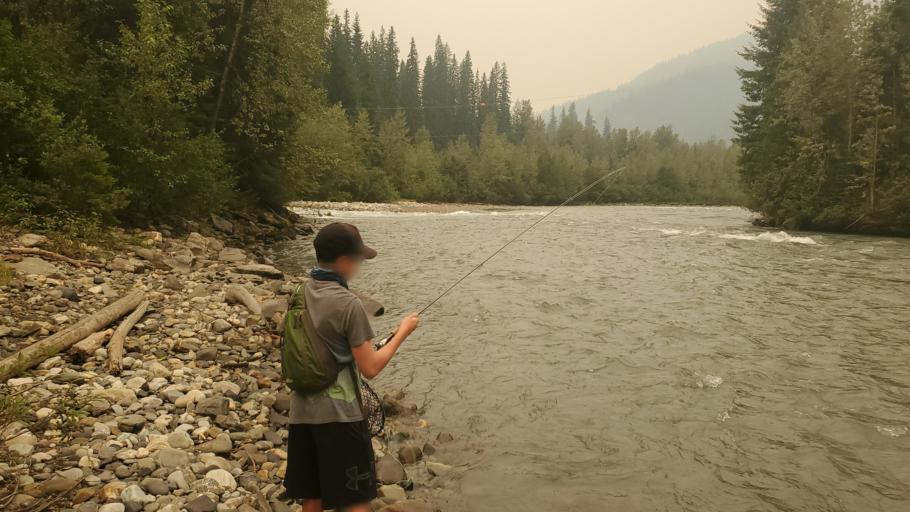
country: CA
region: British Columbia
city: Revelstoke
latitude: 51.1386
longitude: -117.8714
